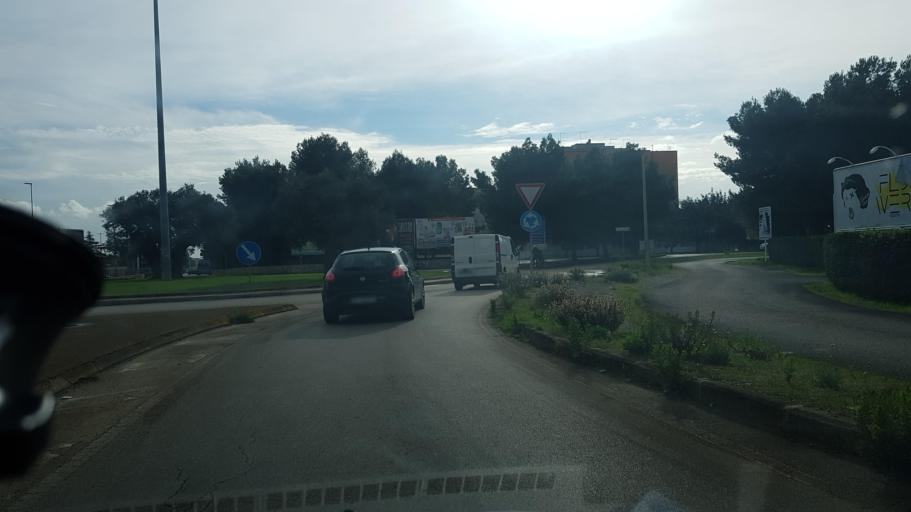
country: IT
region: Apulia
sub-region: Provincia di Brindisi
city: San Vito dei Normanni
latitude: 40.6658
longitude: 17.6987
